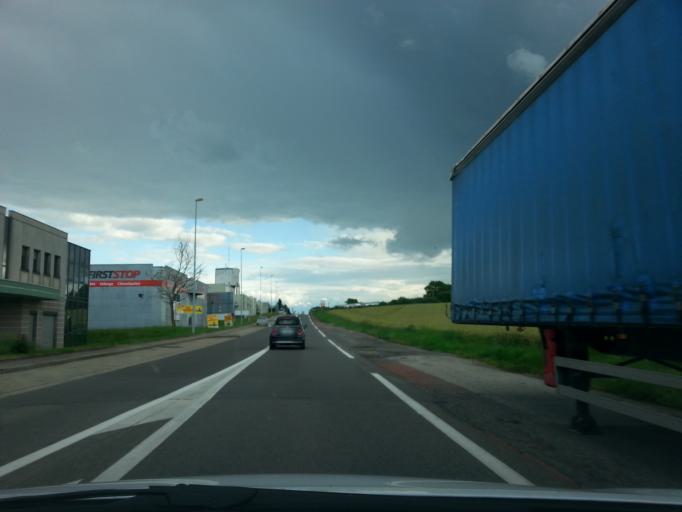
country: FR
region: Rhone-Alpes
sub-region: Departement du Rhone
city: Rillieux-la-Pape
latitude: 45.8288
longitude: 4.9072
